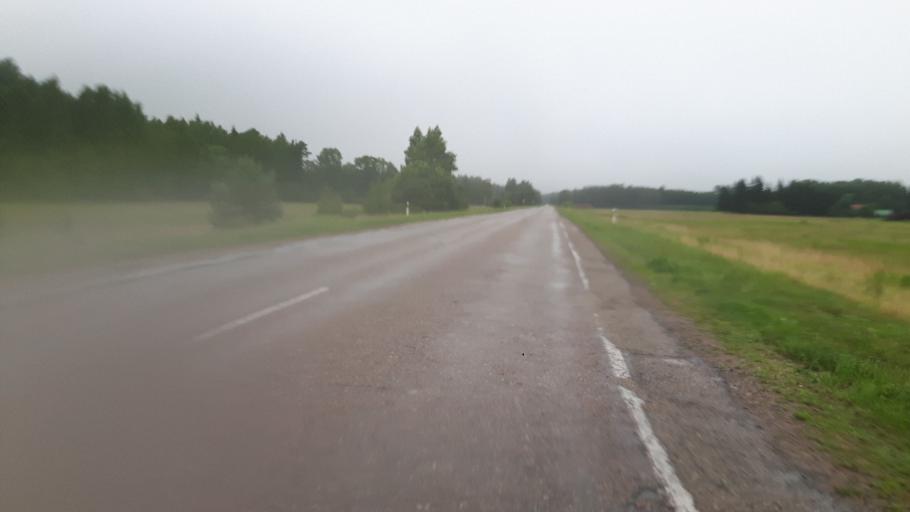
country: LV
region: Rucavas
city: Rucava
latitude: 56.0998
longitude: 21.1330
